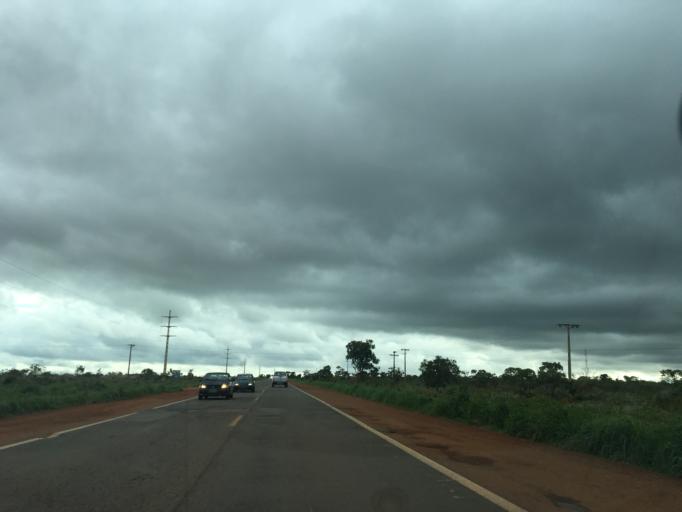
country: BR
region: Federal District
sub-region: Brasilia
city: Brasilia
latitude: -15.9557
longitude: -47.8671
